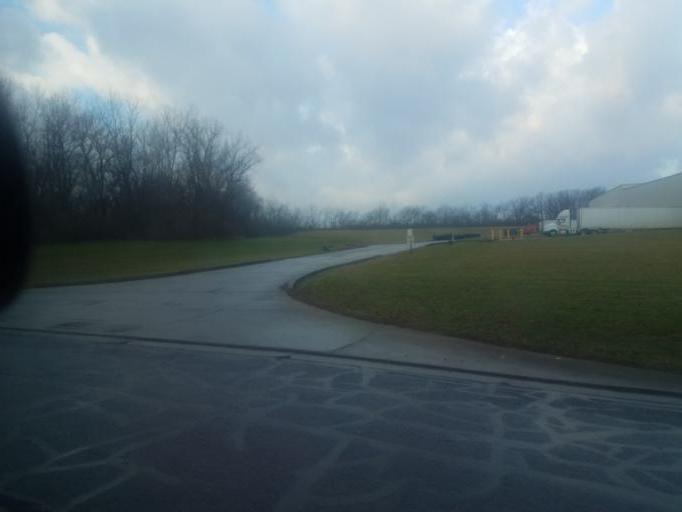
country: US
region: Ohio
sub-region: Marion County
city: Marion
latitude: 40.6064
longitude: -83.1432
